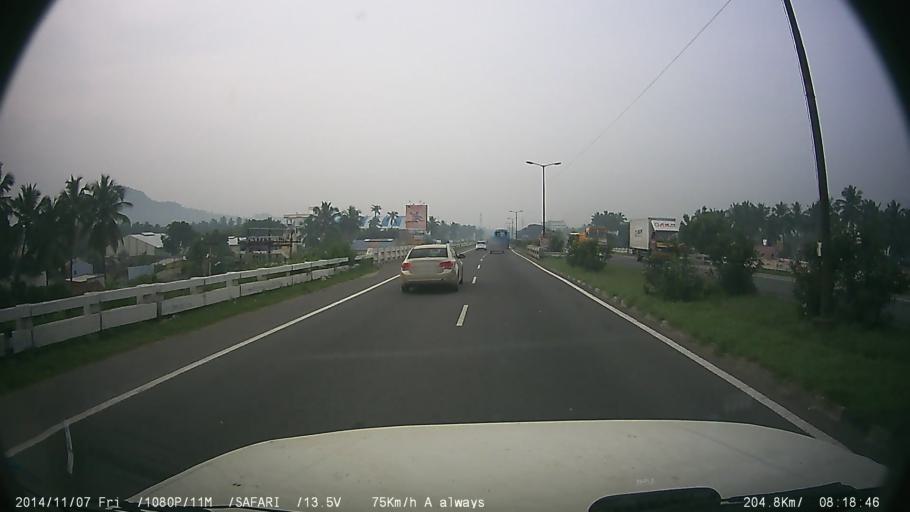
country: IN
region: Tamil Nadu
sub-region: Salem
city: Salem
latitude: 11.6568
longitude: 78.1215
